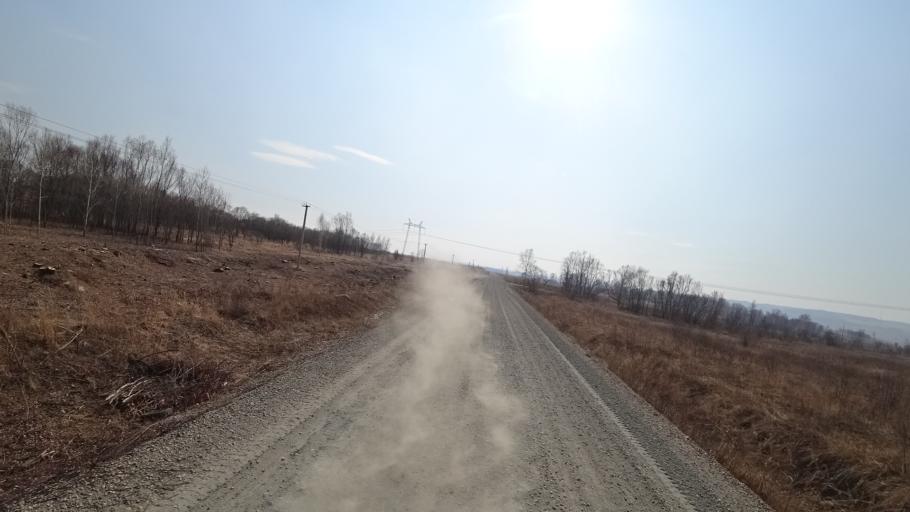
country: RU
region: Amur
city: Novobureyskiy
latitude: 49.8166
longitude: 129.9770
